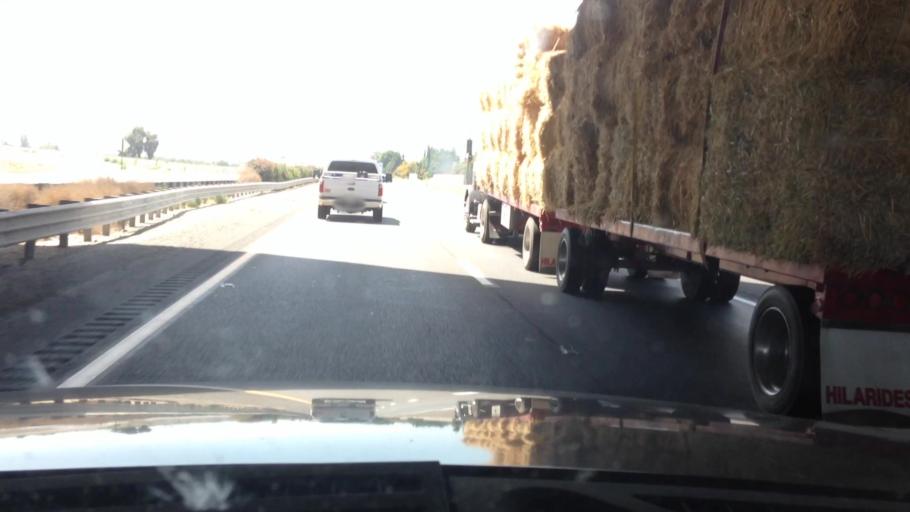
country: US
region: California
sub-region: Tulare County
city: Tulare
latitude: 36.2403
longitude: -119.3453
